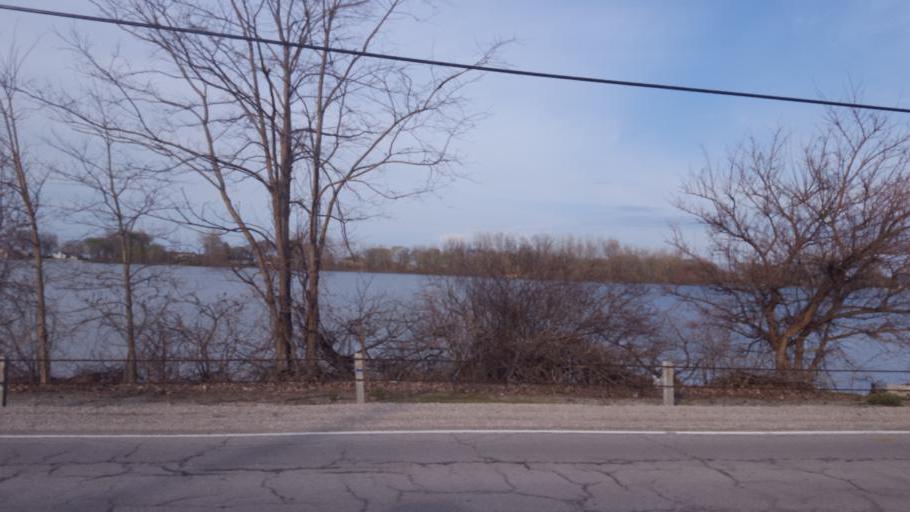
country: US
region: Ohio
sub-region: Erie County
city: Sandusky
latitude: 41.4667
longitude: -82.6741
